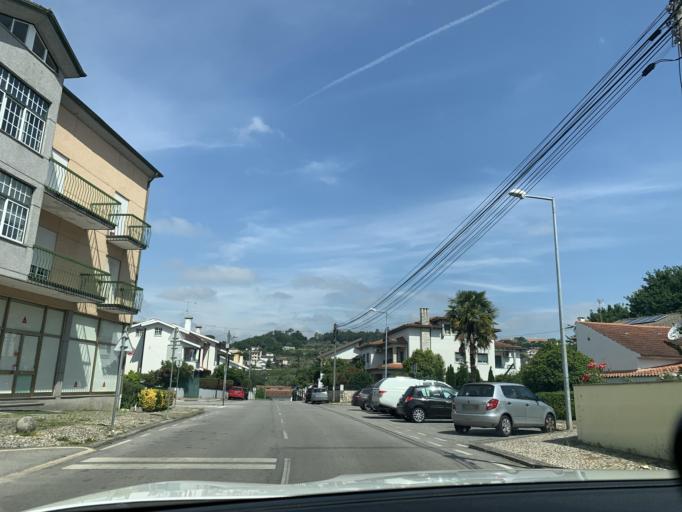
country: PT
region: Viseu
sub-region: Viseu
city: Viseu
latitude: 40.6531
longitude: -7.9341
